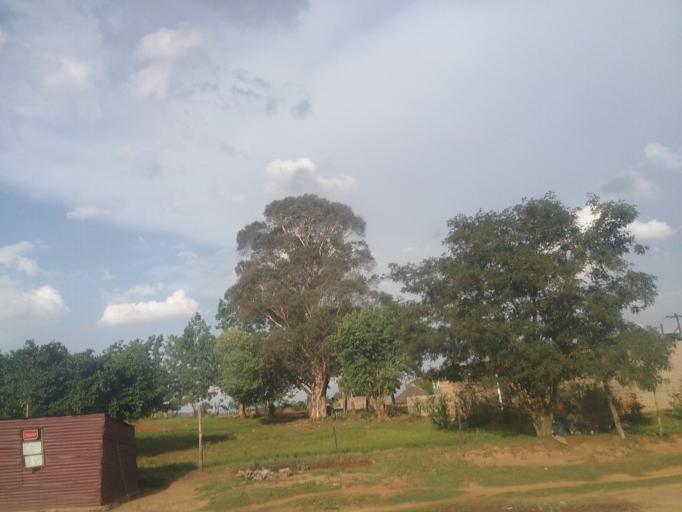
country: LS
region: Leribe
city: Leribe
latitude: -28.9261
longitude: 28.1307
